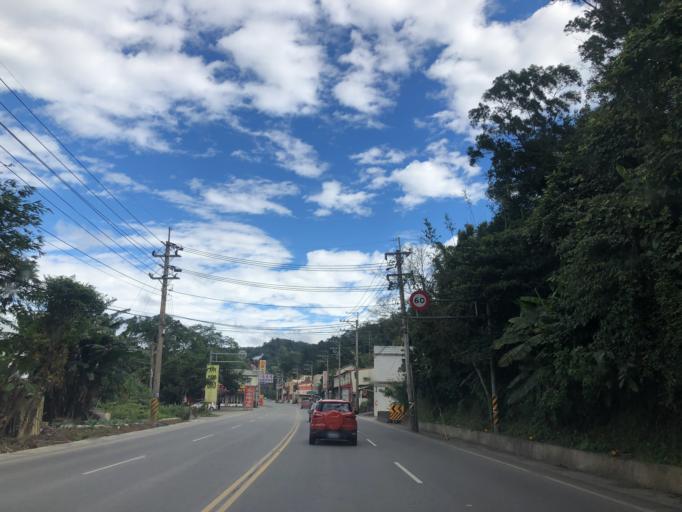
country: TW
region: Taiwan
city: Daxi
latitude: 24.8258
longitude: 121.2648
